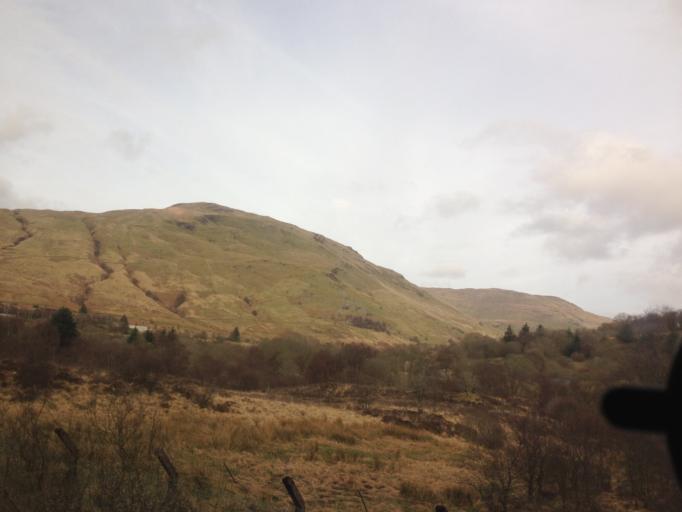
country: GB
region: Scotland
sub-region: Argyll and Bute
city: Garelochhead
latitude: 56.1545
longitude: -4.7804
